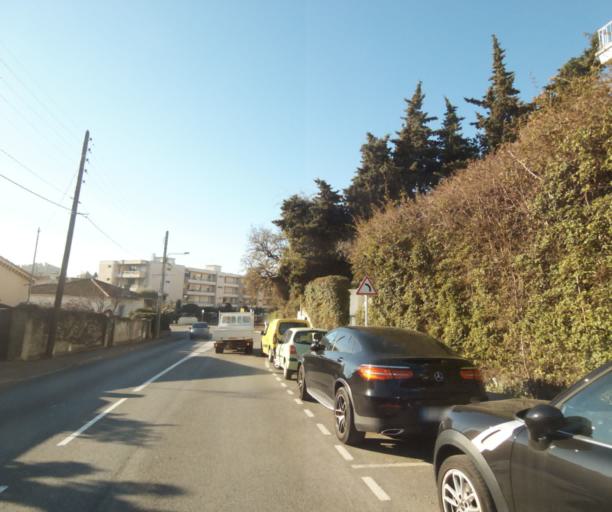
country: FR
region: Provence-Alpes-Cote d'Azur
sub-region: Departement des Alpes-Maritimes
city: Antibes
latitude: 43.5816
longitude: 7.1099
